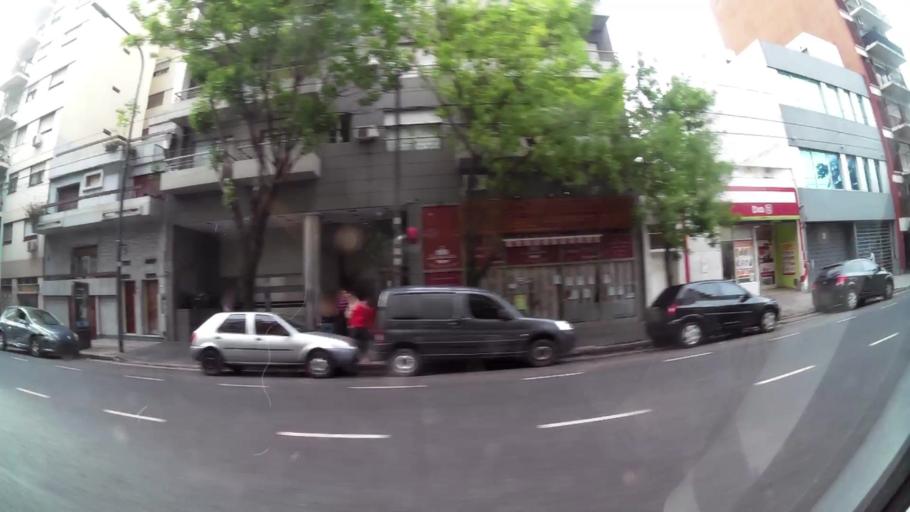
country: AR
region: Buenos Aires F.D.
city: Buenos Aires
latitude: -34.6265
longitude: -58.4247
